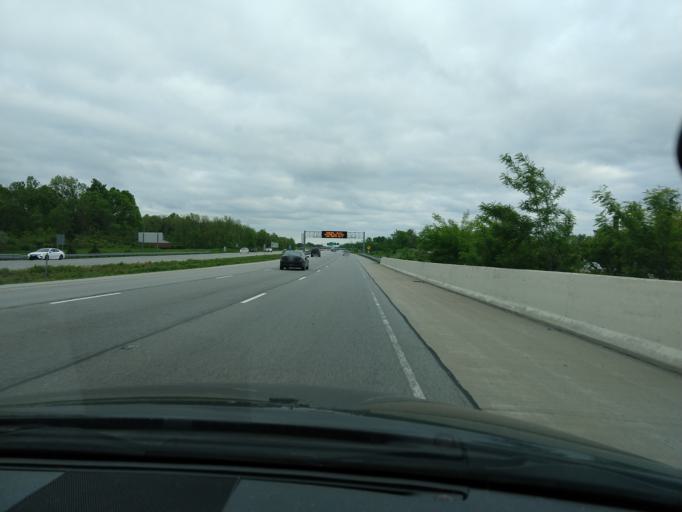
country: US
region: Indiana
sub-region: Hamilton County
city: Westfield
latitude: 40.0302
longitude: -86.1349
